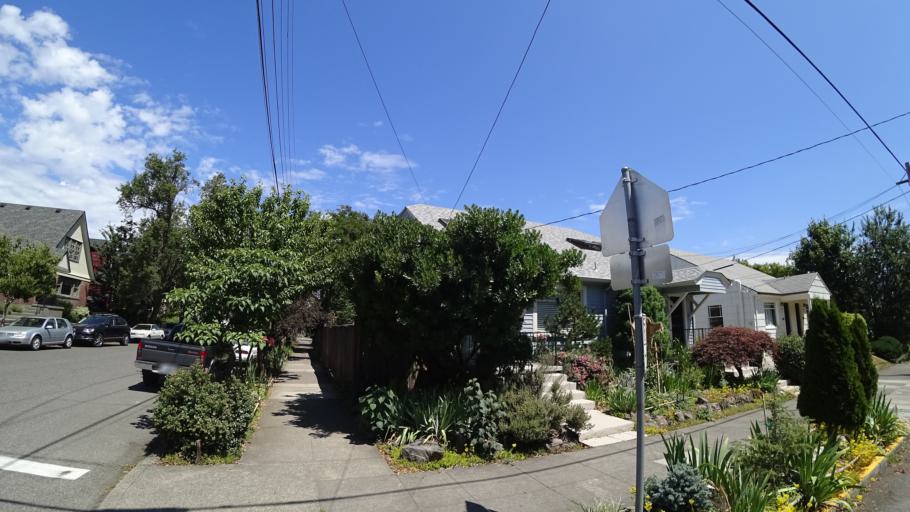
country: US
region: Oregon
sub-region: Multnomah County
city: Portland
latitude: 45.5340
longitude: -122.7066
